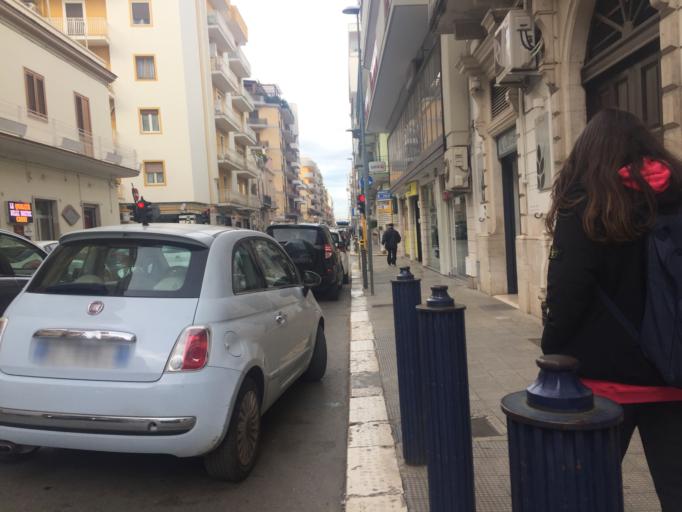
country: IT
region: Apulia
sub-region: Provincia di Bari
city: Bitonto
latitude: 41.1103
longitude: 16.6884
